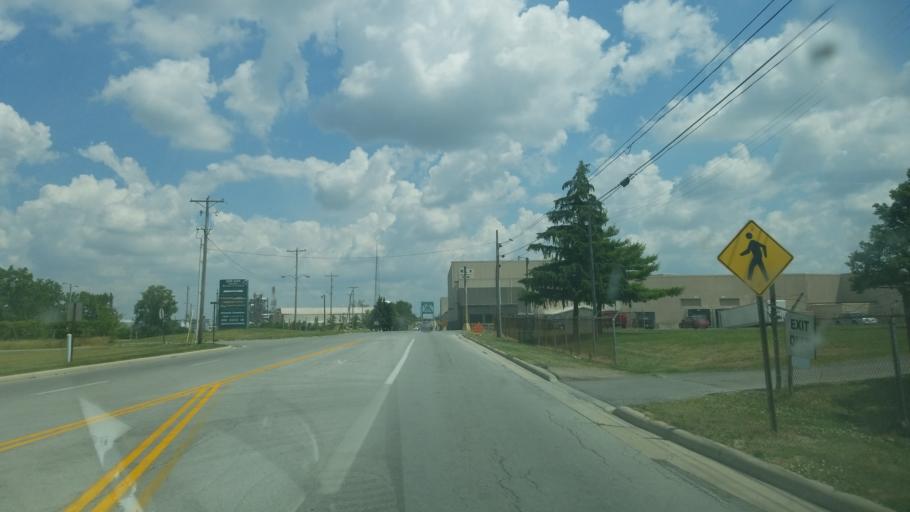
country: US
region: Ohio
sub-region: Allen County
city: Lima
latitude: 40.7125
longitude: -84.1166
